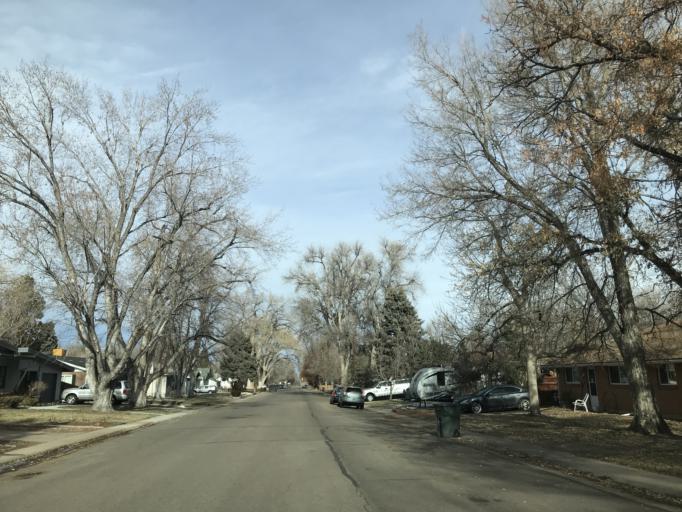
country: US
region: Colorado
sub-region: Arapahoe County
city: Littleton
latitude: 39.6044
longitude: -105.0116
